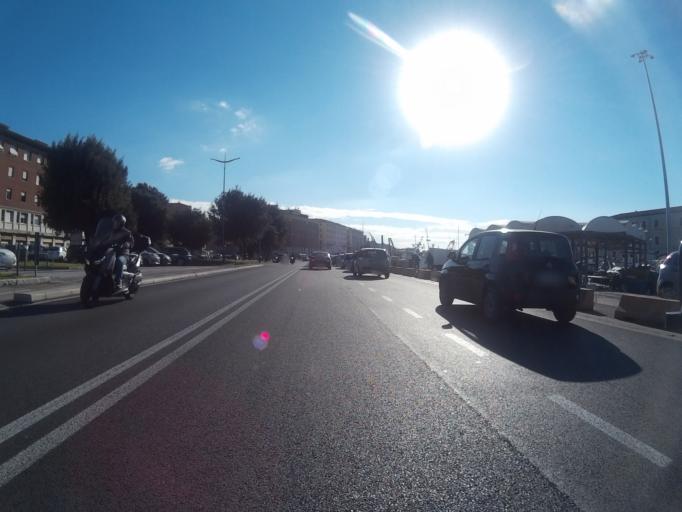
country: IT
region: Tuscany
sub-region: Provincia di Livorno
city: Livorno
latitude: 43.5509
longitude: 10.3042
